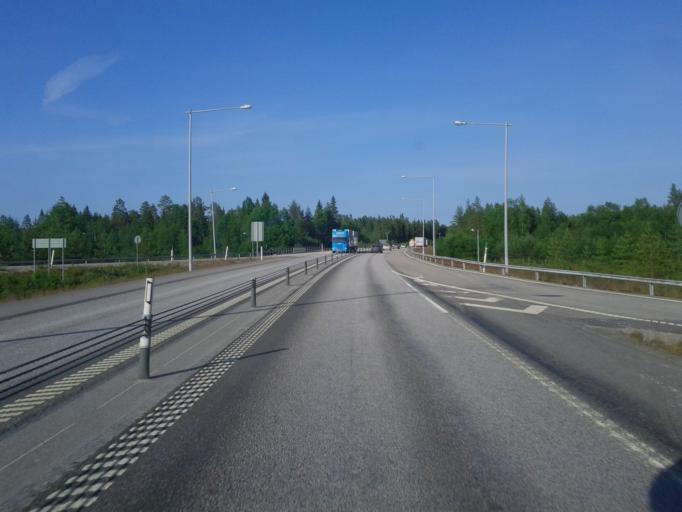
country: SE
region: Vaesterbotten
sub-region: Umea Kommun
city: Saevar
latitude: 63.8930
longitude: 20.5266
